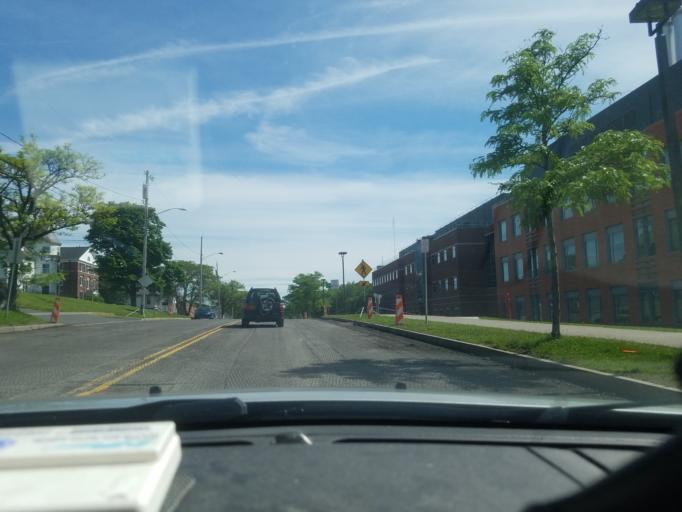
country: US
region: New York
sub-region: Onondaga County
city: Syracuse
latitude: 43.0380
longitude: -76.1300
